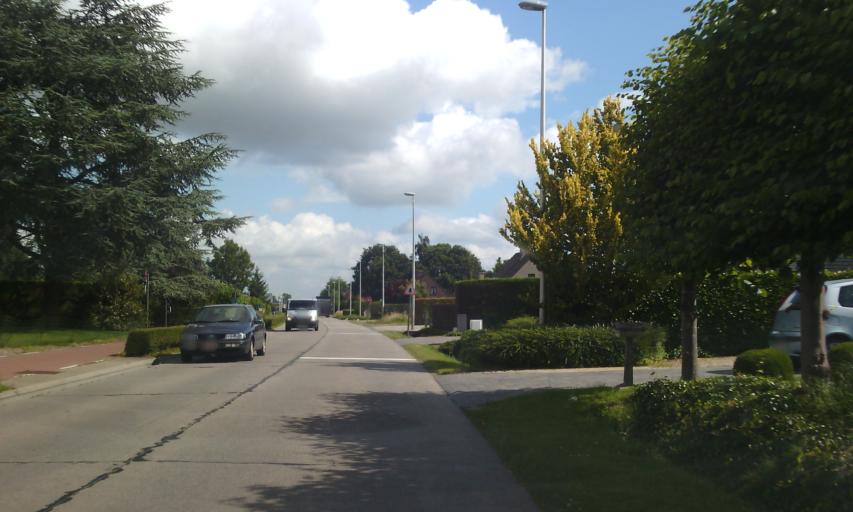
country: BE
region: Flanders
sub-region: Provincie Oost-Vlaanderen
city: Lokeren
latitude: 51.1157
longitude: 3.9627
